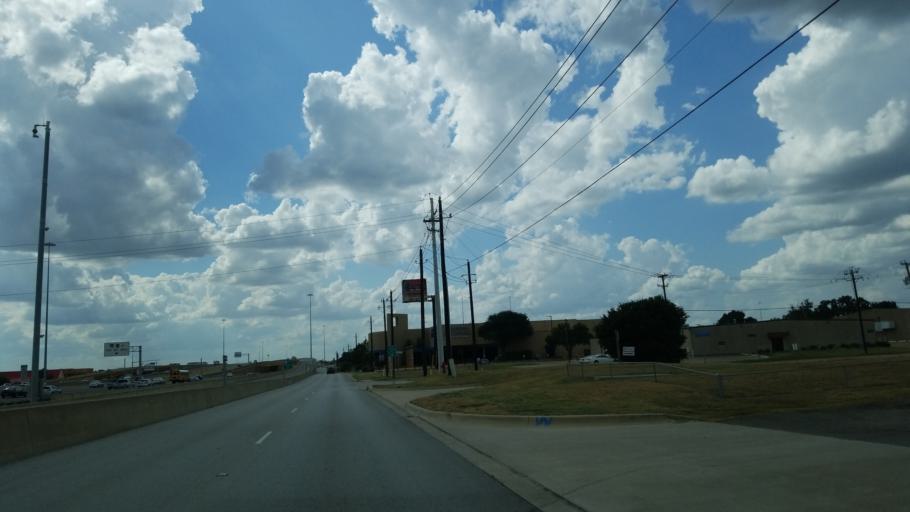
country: US
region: Texas
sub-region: Tarrant County
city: Euless
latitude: 32.8385
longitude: -97.1065
